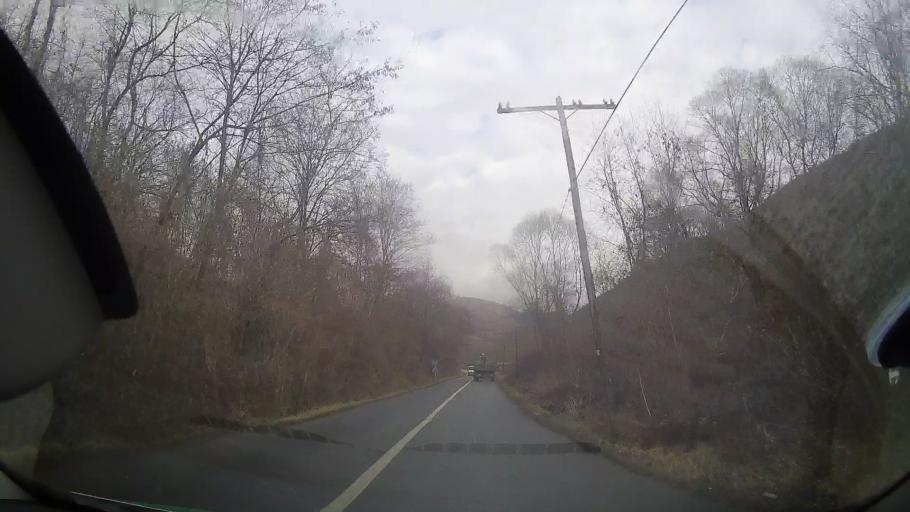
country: RO
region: Alba
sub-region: Comuna Ocolis
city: Ocolis
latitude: 46.4556
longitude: 23.4684
